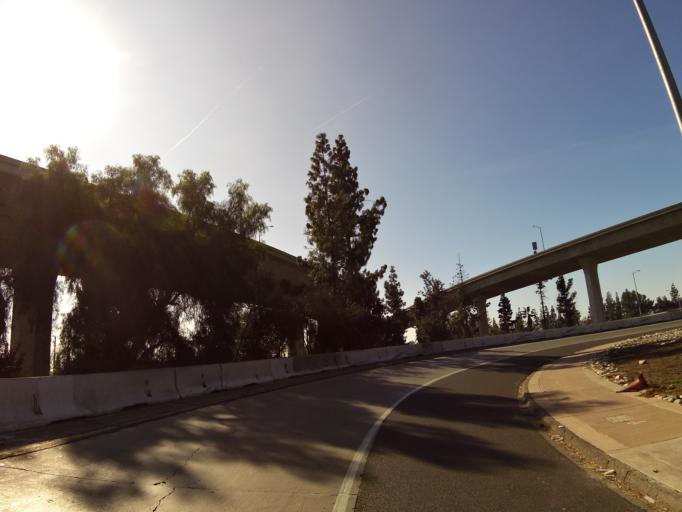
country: US
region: California
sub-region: Los Angeles County
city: San Fernando
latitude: 34.2651
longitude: -118.4707
